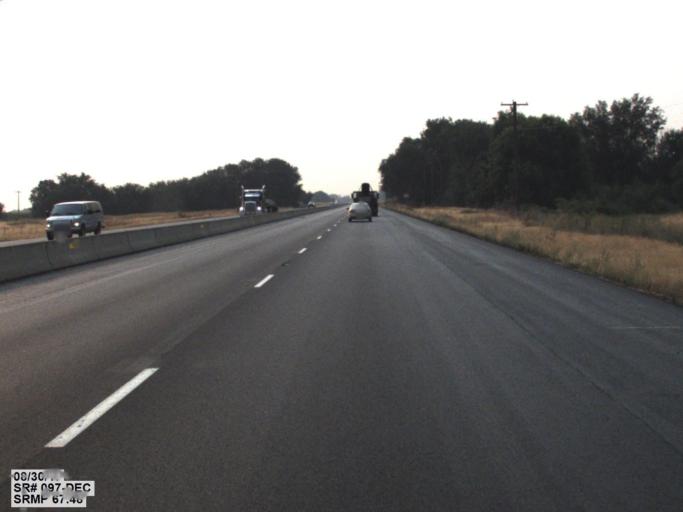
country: US
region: Washington
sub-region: Yakima County
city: Wapato
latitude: 46.4291
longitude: -120.4128
